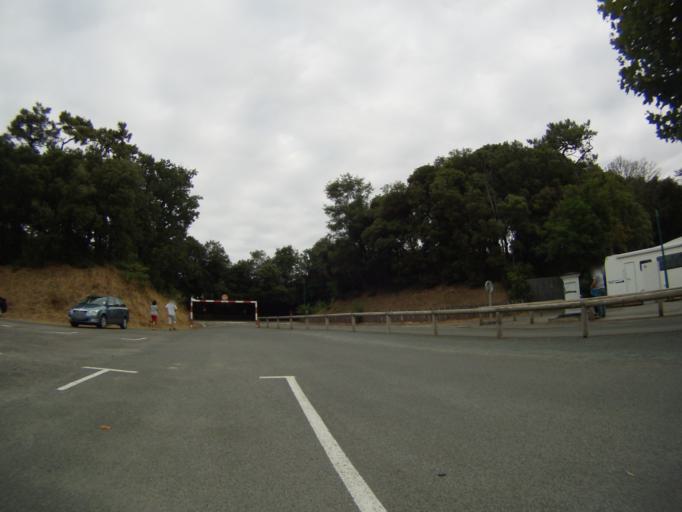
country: FR
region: Pays de la Loire
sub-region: Departement de la Vendee
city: Longeville-sur-Mer
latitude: 46.4032
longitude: -1.5058
